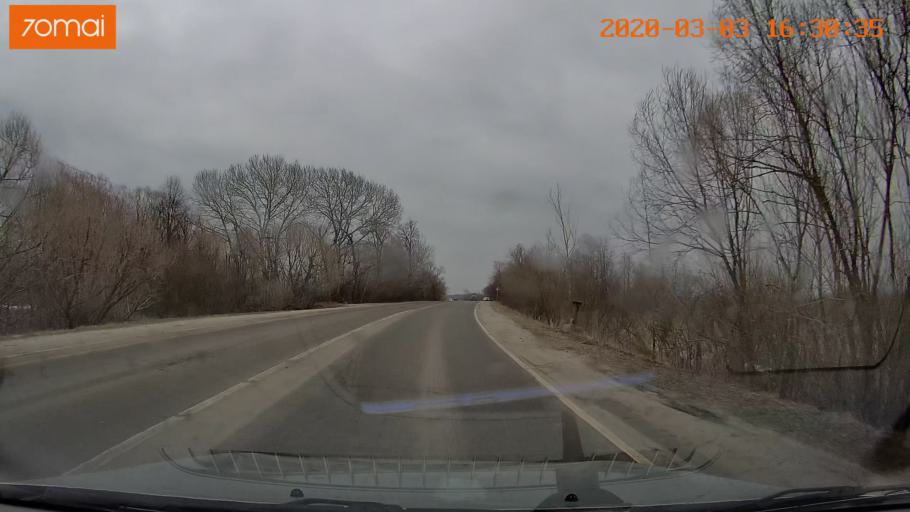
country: RU
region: Moskovskaya
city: Konobeyevo
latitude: 55.4322
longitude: 38.7131
